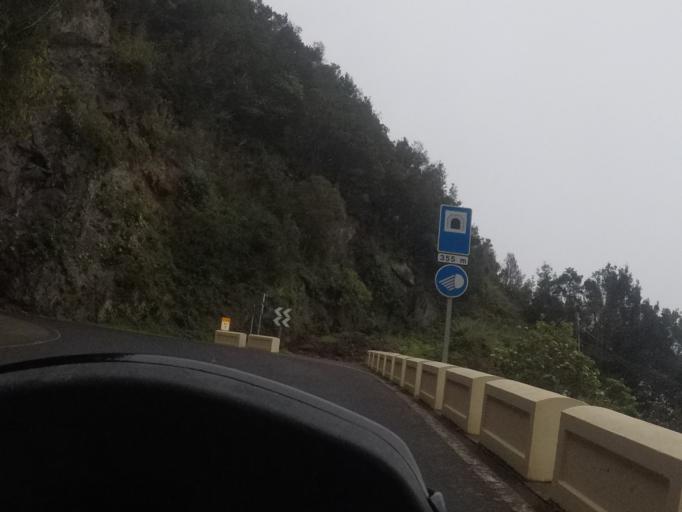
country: ES
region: Canary Islands
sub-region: Provincia de Santa Cruz de Tenerife
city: Santa Cruz de Tenerife
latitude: 28.5511
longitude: -16.2054
